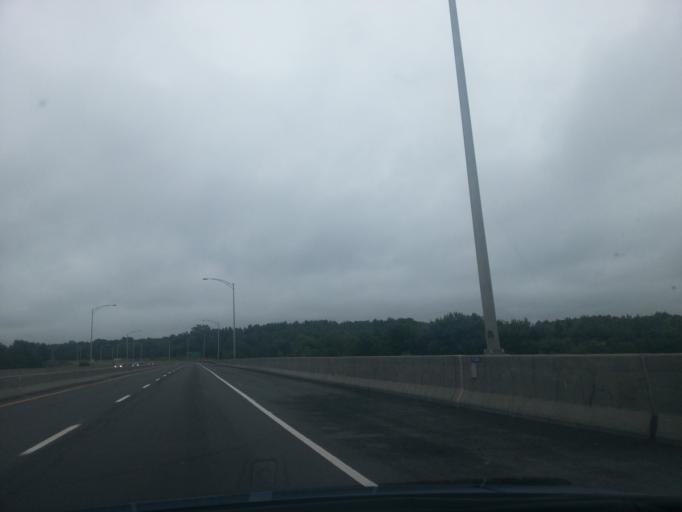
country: CA
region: Quebec
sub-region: Centre-du-Quebec
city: Drummondville
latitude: 45.9107
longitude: -72.5045
